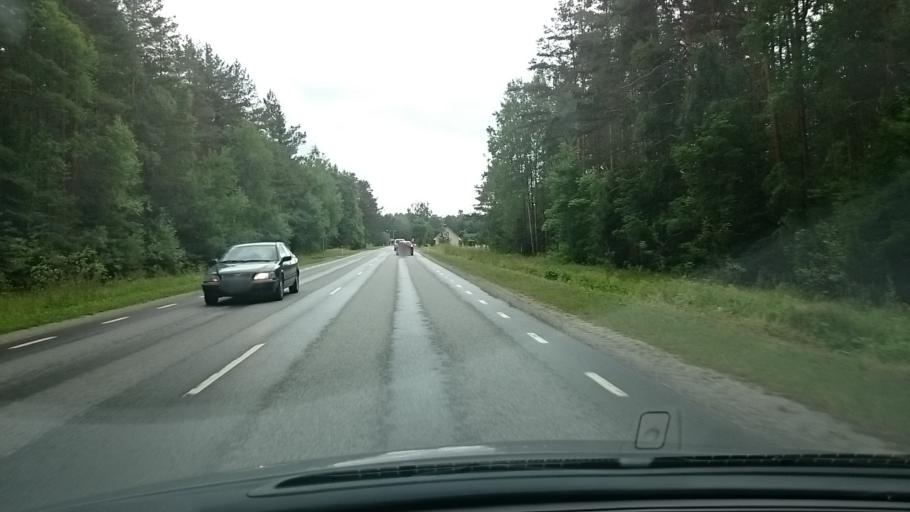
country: EE
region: Harju
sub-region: Nissi vald
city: Riisipere
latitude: 59.2424
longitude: 24.2773
